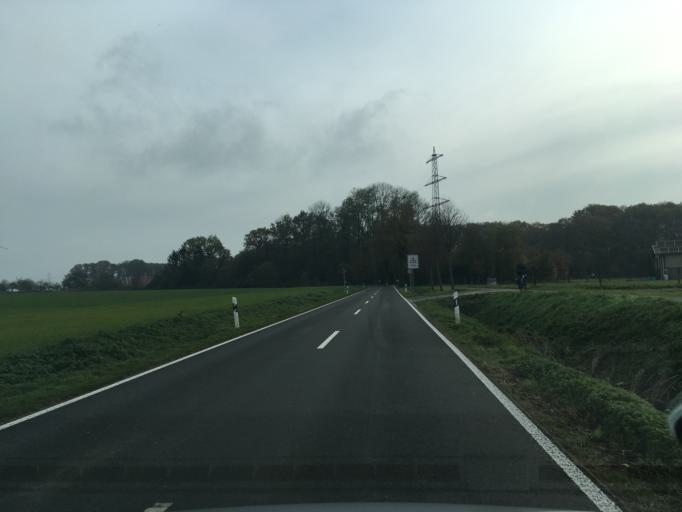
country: DE
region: North Rhine-Westphalia
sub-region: Regierungsbezirk Munster
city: Velen
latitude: 51.9305
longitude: 6.9475
